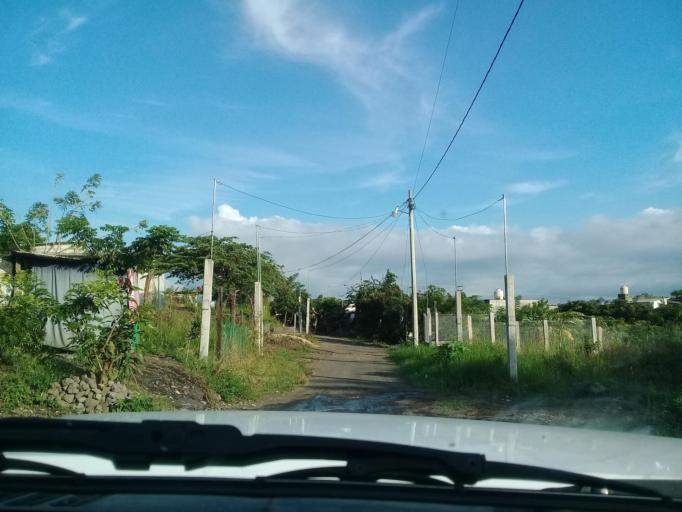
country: MX
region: Veracruz
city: Catemaco
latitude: 18.4258
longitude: -95.1021
